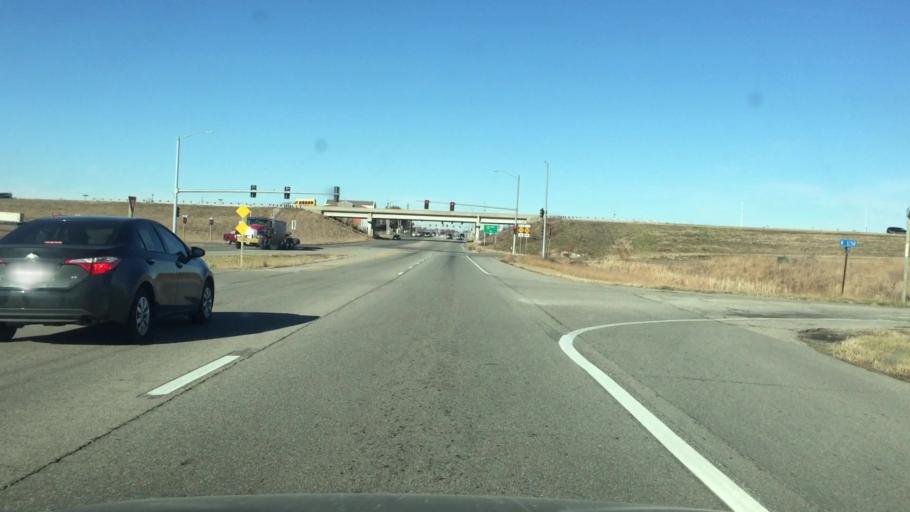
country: US
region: Kansas
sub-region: Douglas County
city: Lawrence
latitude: 38.9179
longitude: -95.2604
